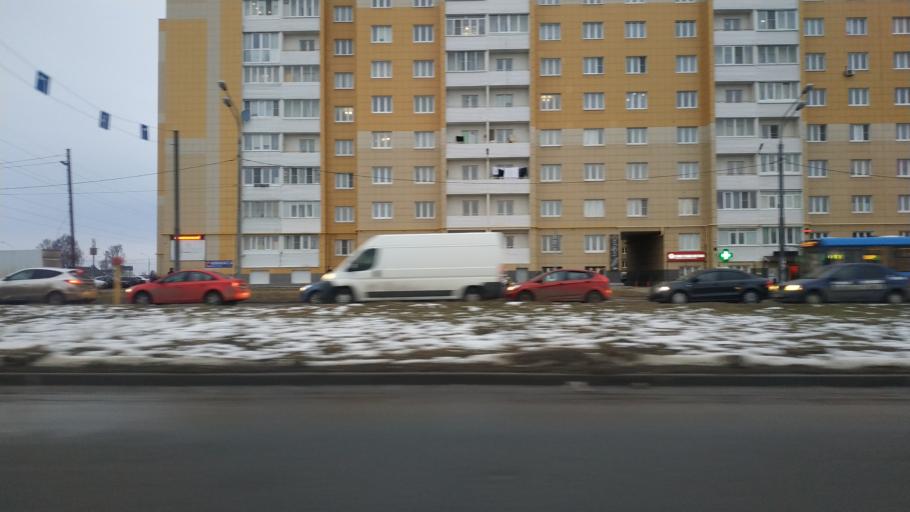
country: RU
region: Tverskaya
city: Tver
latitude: 56.8175
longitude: 35.8857
